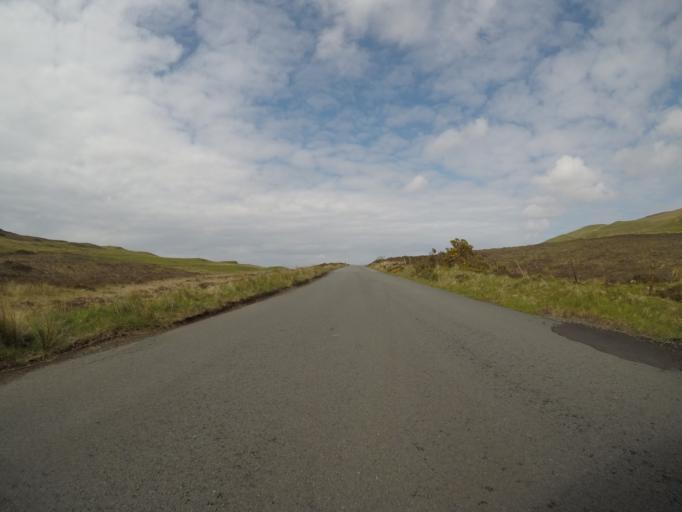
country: GB
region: Scotland
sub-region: Highland
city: Portree
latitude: 57.5965
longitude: -6.3750
